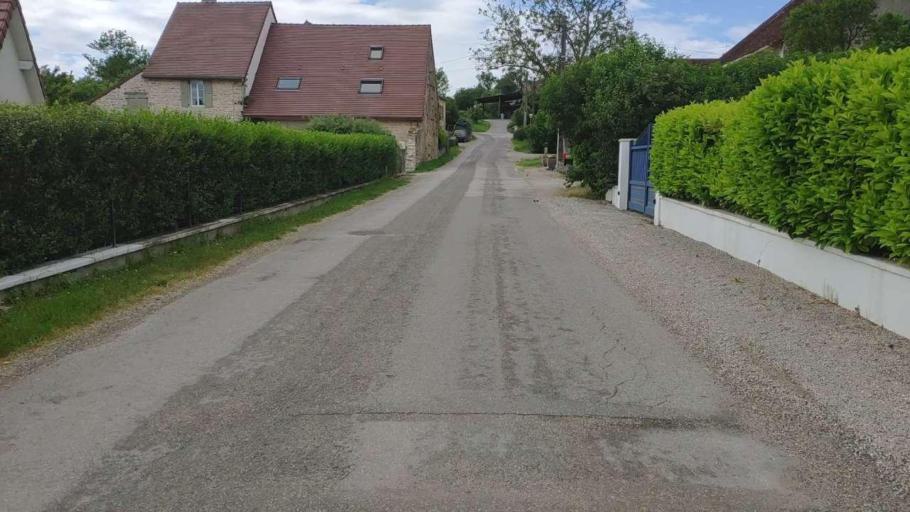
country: FR
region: Franche-Comte
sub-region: Departement du Jura
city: Montmorot
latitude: 46.7341
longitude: 5.5194
